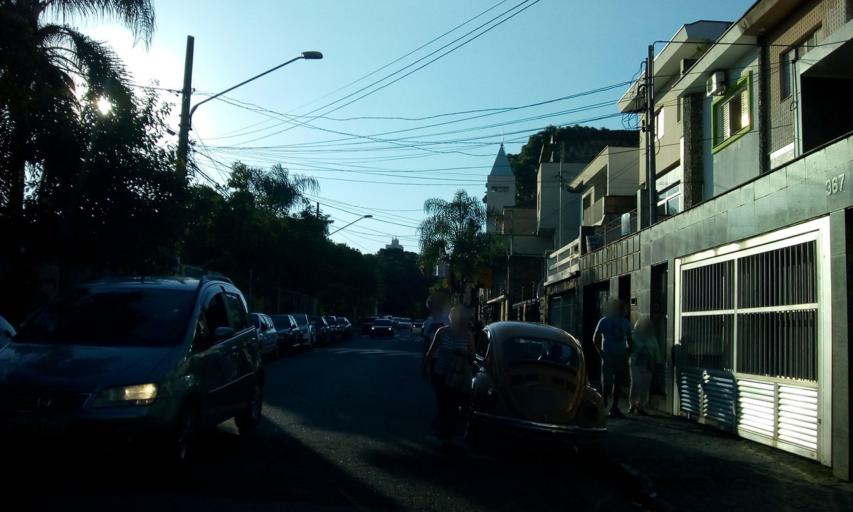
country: BR
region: Sao Paulo
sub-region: Sao Paulo
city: Sao Paulo
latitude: -23.4929
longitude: -46.6153
